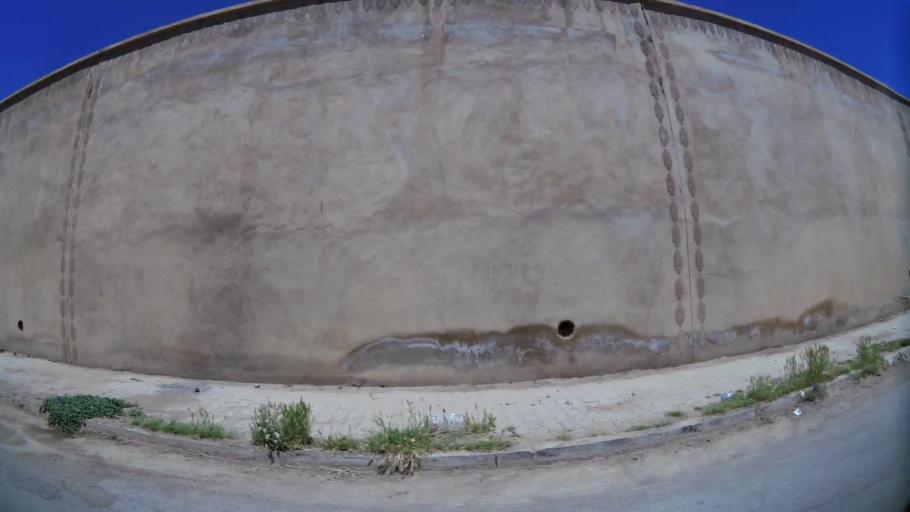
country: MA
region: Oriental
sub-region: Oujda-Angad
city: Oujda
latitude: 34.6575
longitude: -1.9505
